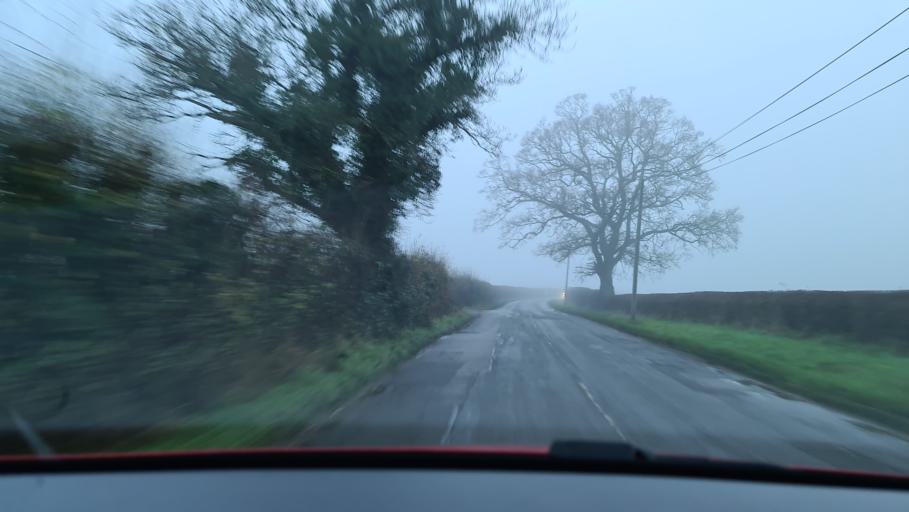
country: GB
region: England
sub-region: Buckinghamshire
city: Waddesdon
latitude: 51.8690
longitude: -0.9025
